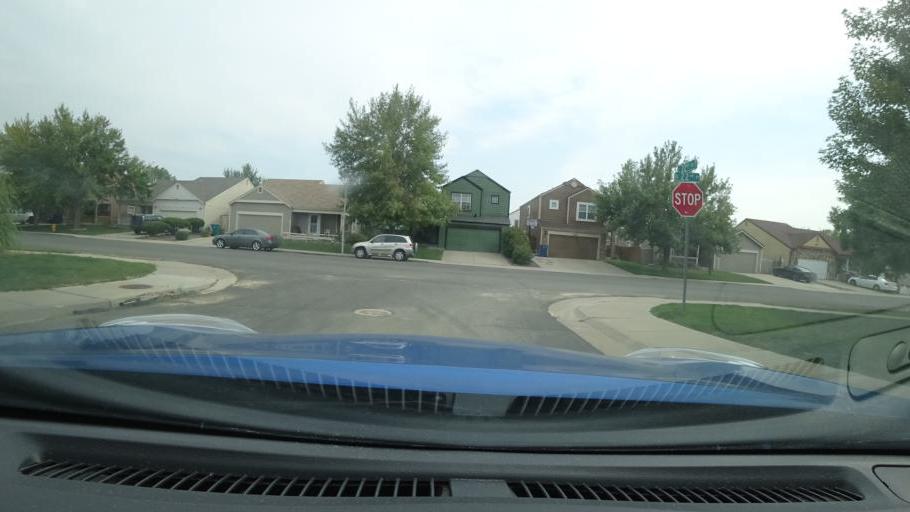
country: US
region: Colorado
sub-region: Adams County
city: Aurora
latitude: 39.7507
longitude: -104.7664
